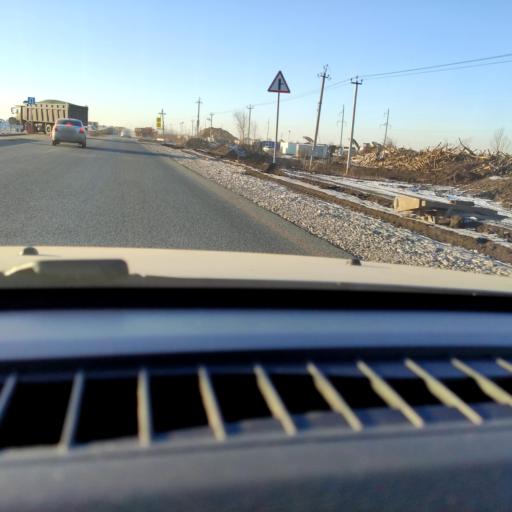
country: RU
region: Samara
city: Podstepki
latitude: 53.5606
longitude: 49.2051
